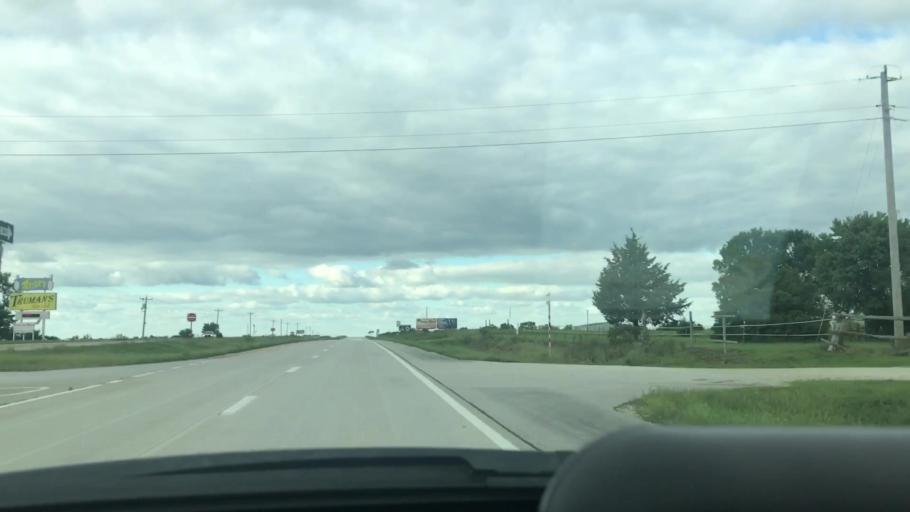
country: US
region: Missouri
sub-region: Benton County
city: Lincoln
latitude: 38.3402
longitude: -93.3406
